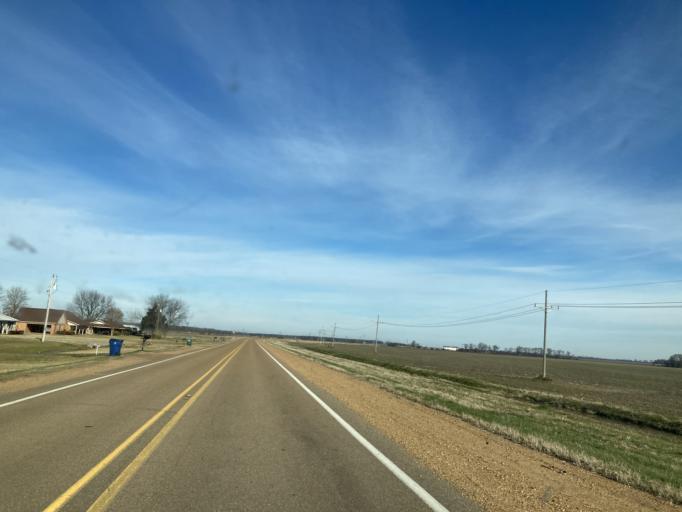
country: US
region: Mississippi
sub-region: Humphreys County
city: Belzoni
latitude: 32.9871
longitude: -90.5878
